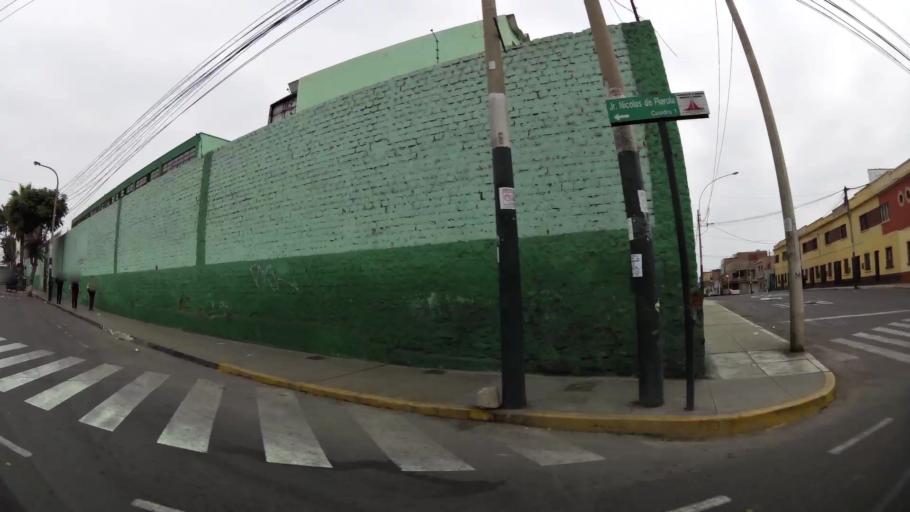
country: PE
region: Callao
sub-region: Callao
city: Callao
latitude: -12.0604
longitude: -77.1303
